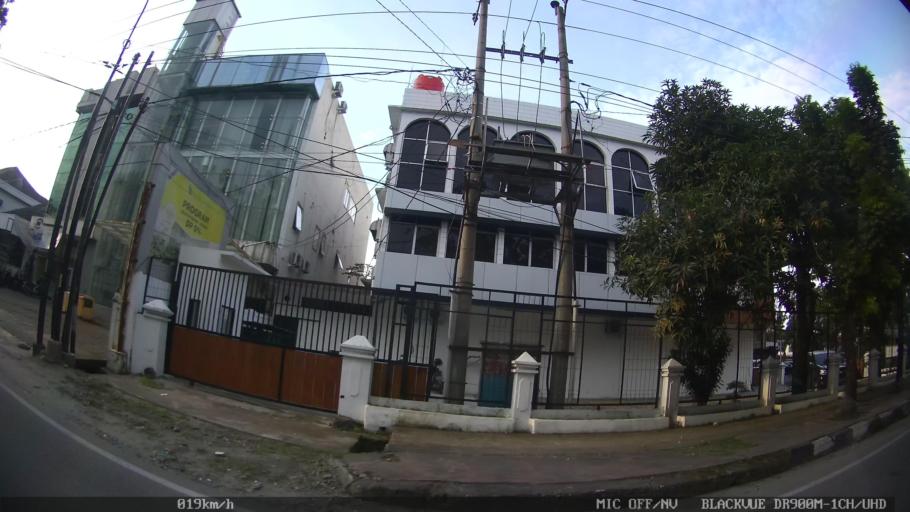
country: ID
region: North Sumatra
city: Medan
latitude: 3.5768
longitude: 98.6606
